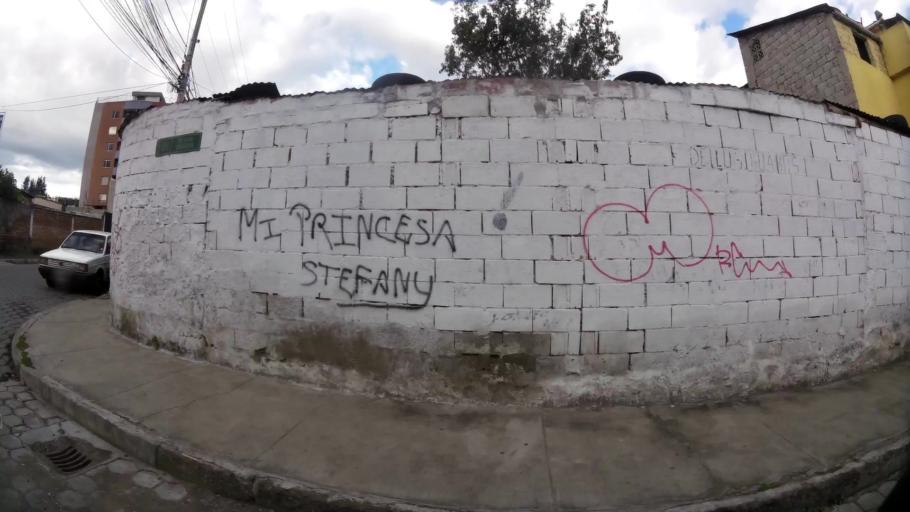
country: EC
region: Pichincha
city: Quito
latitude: -0.1451
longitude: -78.4706
